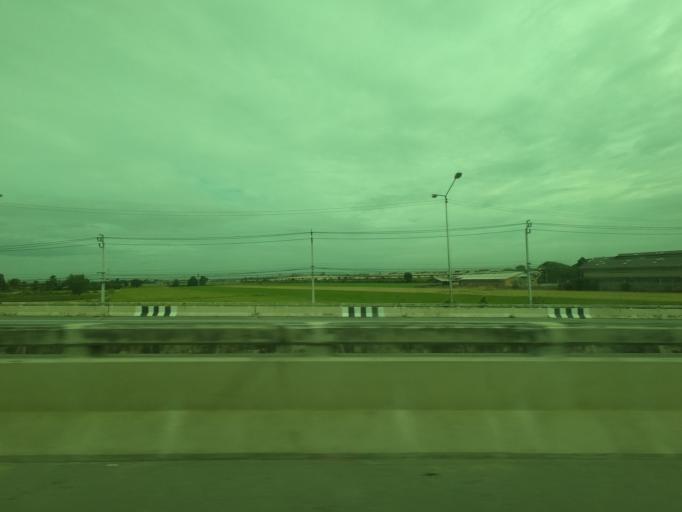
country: TH
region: Nonthaburi
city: Bang Bua Thong
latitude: 13.9454
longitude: 100.4328
